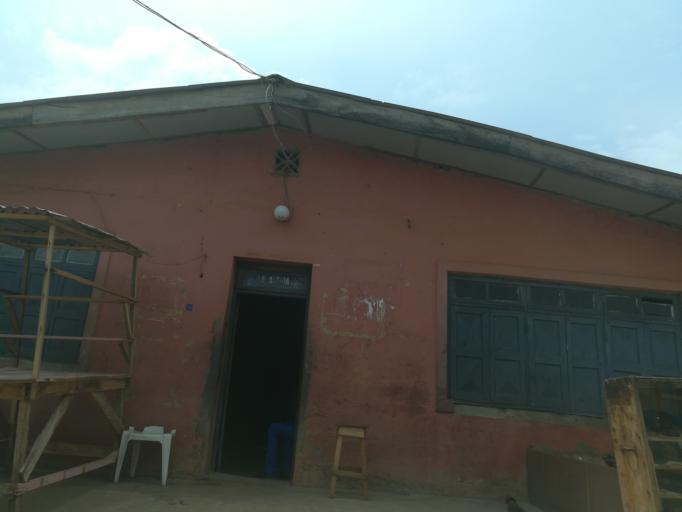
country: NG
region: Lagos
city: Ikorodu
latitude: 6.6095
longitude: 3.5067
